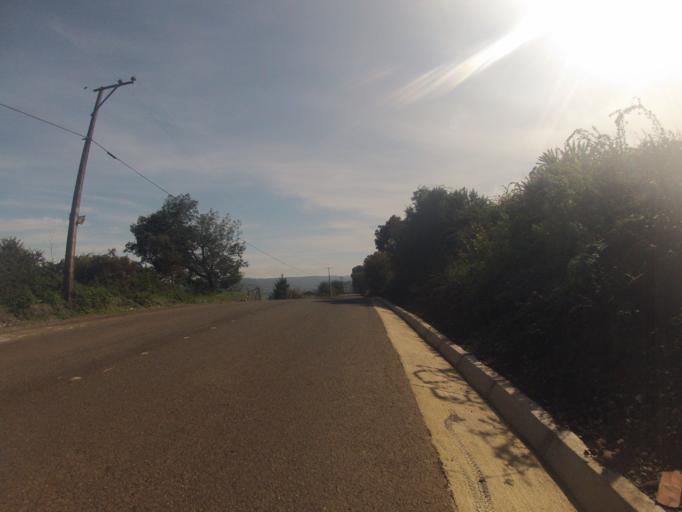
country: CL
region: Araucania
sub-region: Provincia de Cautin
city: Temuco
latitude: -38.7177
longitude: -72.5988
